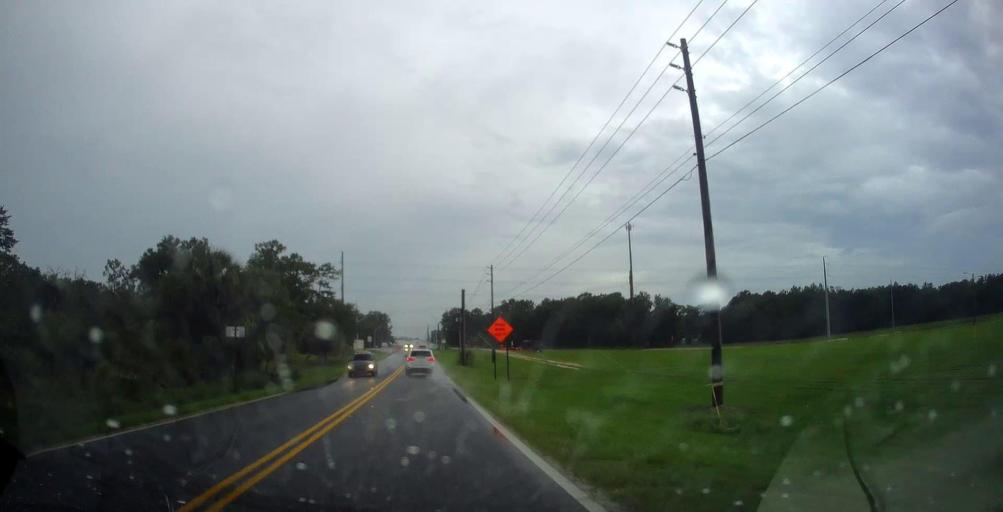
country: US
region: Florida
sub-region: Marion County
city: Ocala
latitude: 29.2170
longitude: -82.0869
